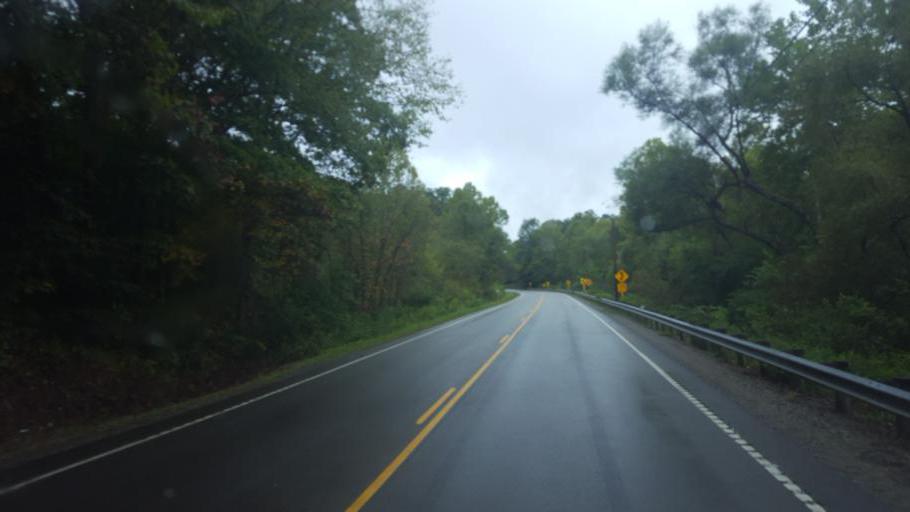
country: US
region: Ohio
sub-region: Jackson County
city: Oak Hill
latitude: 38.8415
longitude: -82.6382
